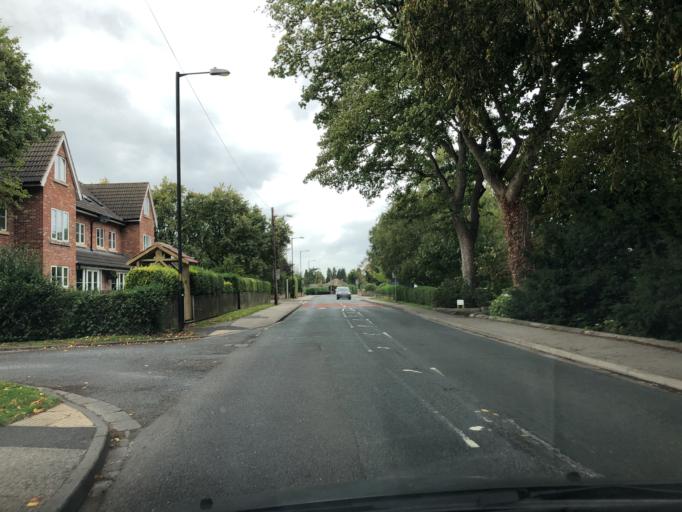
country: GB
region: England
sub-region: North Yorkshire
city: Ripon
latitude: 54.1272
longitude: -1.5275
